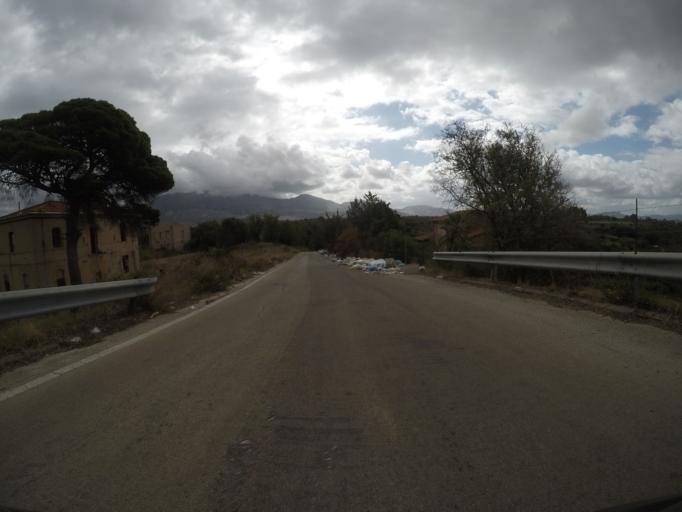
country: IT
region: Sicily
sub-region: Palermo
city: Partinico
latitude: 38.0833
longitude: 13.1084
